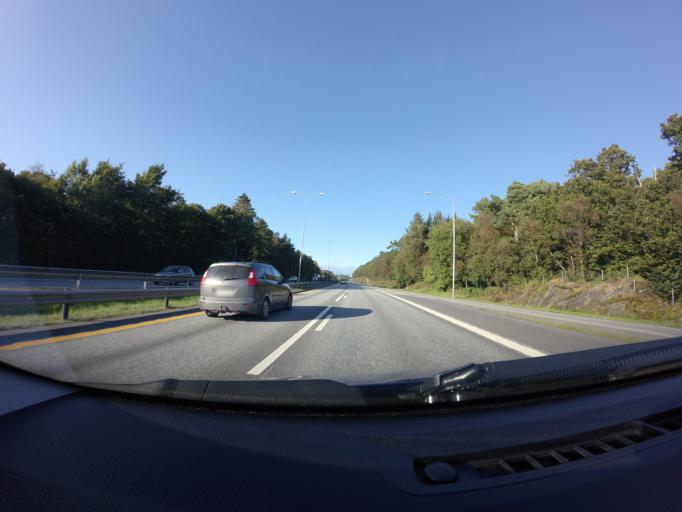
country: NO
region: Rogaland
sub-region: Stavanger
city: Stavanger
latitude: 58.9239
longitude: 5.7076
